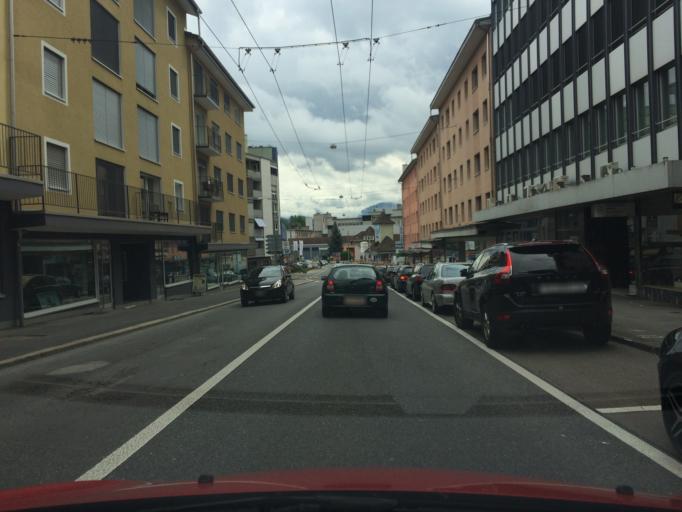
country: CH
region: Lucerne
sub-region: Hochdorf District
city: Emmen
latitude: 47.0743
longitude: 8.2770
